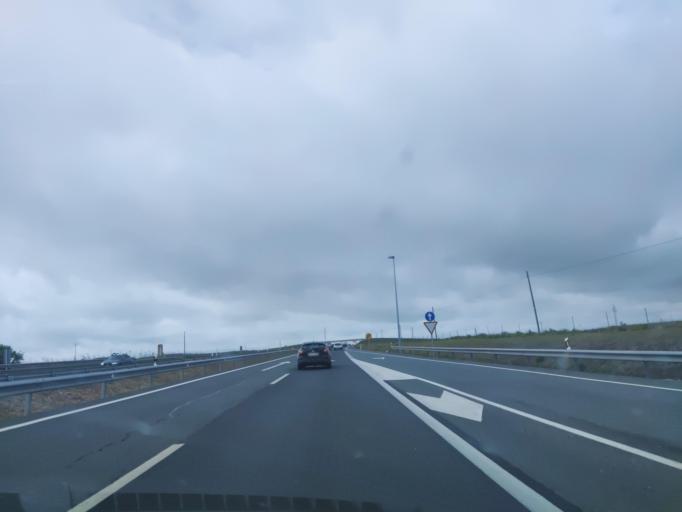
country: ES
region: Castille-La Mancha
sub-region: Province of Toledo
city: Cabanas de la Sagra
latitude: 40.0204
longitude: -3.9422
